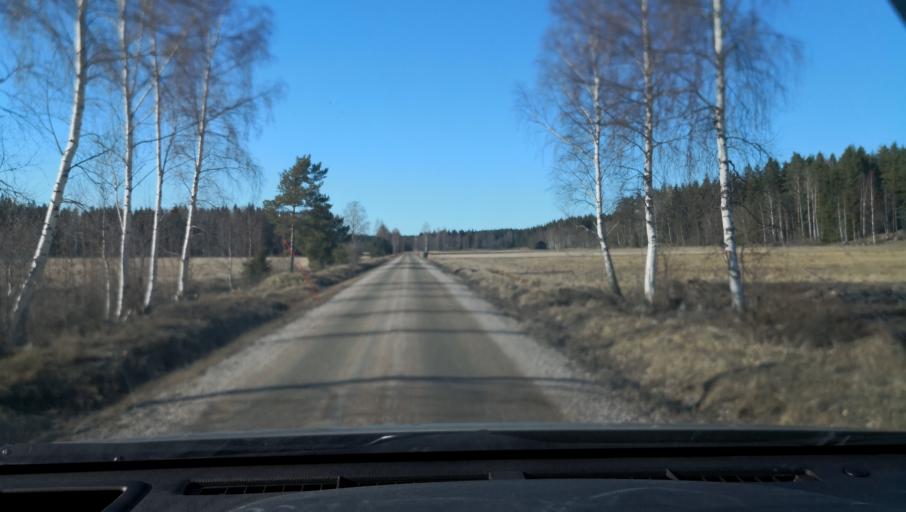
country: SE
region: Vaestmanland
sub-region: Sala Kommun
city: Sala
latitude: 60.1259
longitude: 16.6556
